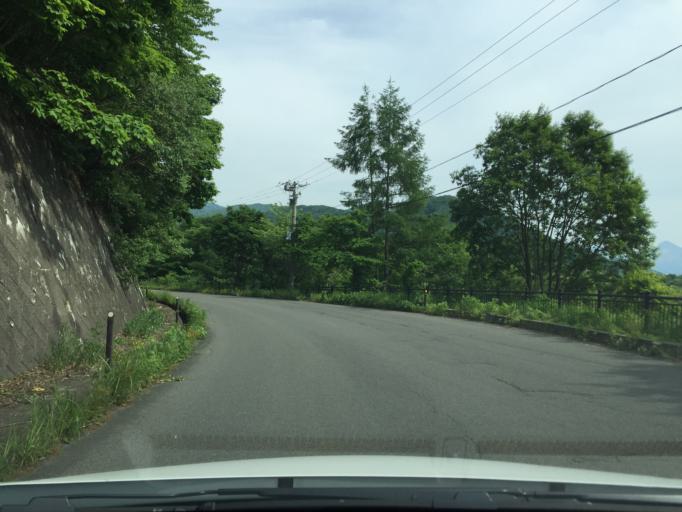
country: JP
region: Fukushima
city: Inawashiro
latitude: 37.7290
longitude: 140.0556
